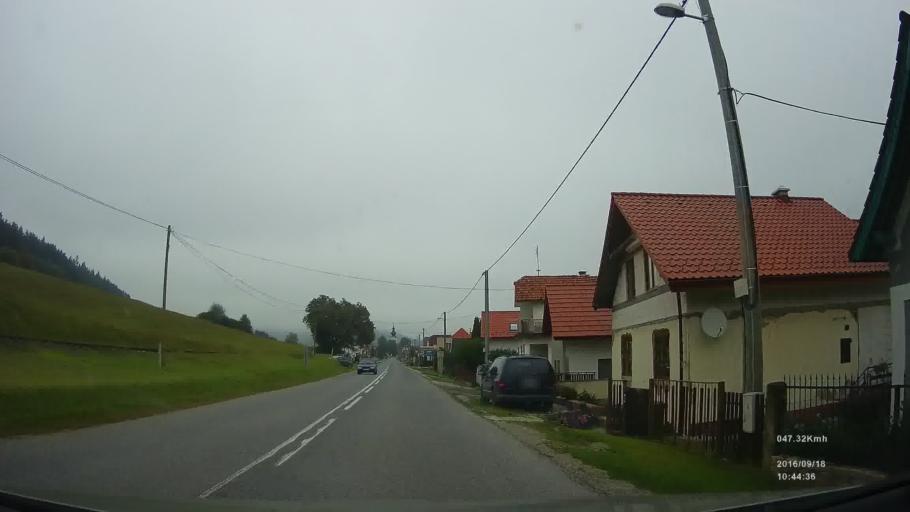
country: SK
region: Kosicky
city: Spisska Nova Ves
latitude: 48.9562
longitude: 20.5840
